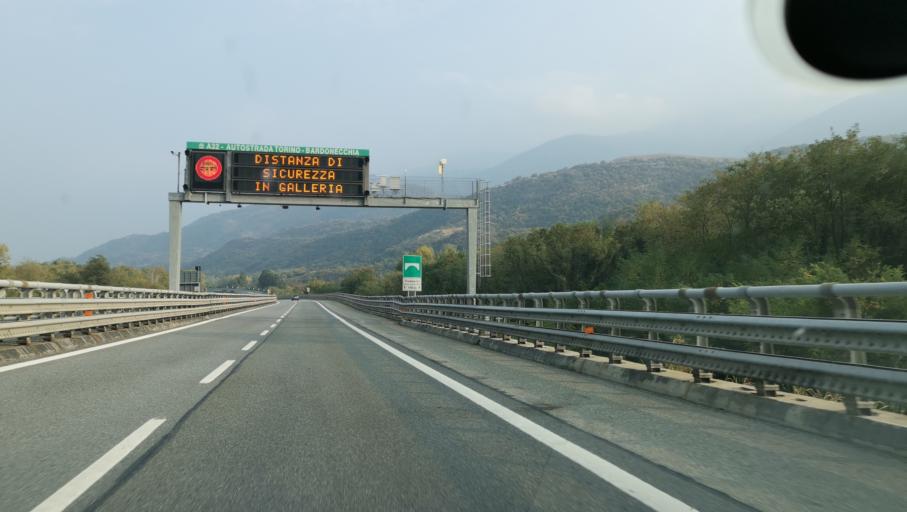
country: IT
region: Piedmont
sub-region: Provincia di Torino
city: Mattie
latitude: 45.1345
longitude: 7.0955
